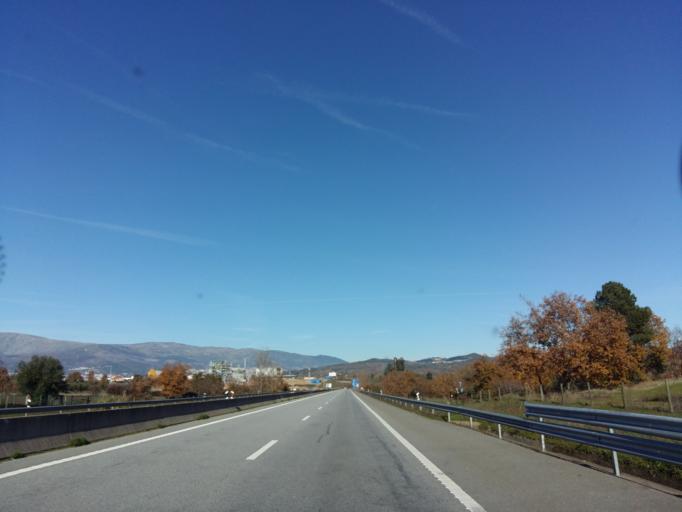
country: PT
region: Castelo Branco
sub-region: Concelho do Fundao
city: Fundao
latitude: 40.1616
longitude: -7.4856
